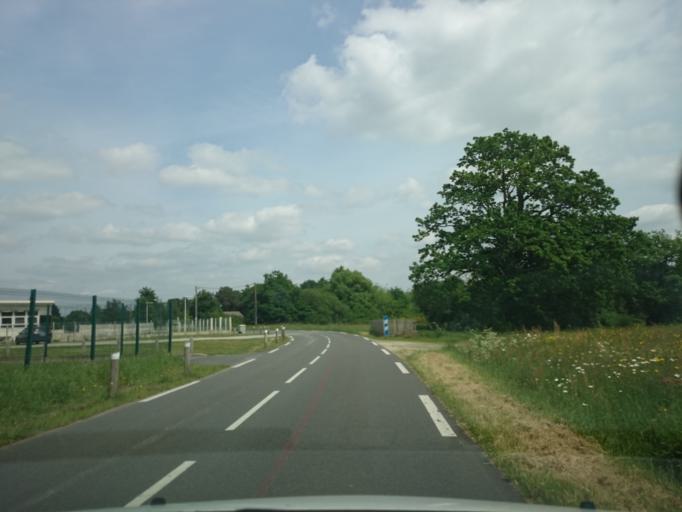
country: FR
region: Pays de la Loire
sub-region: Departement de la Loire-Atlantique
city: La Chevroliere
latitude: 47.1230
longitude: -1.6300
